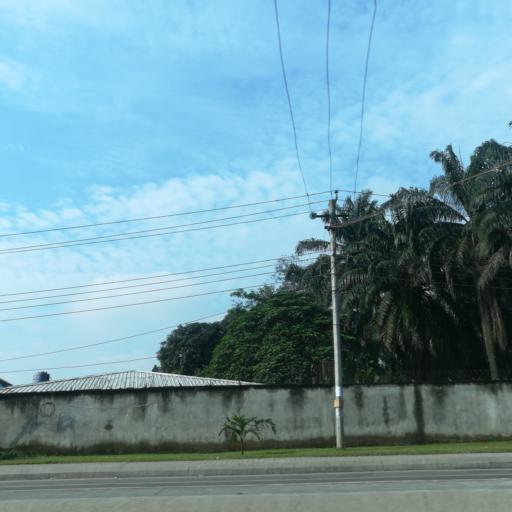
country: NG
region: Rivers
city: Port Harcourt
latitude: 4.8082
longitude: 7.0205
